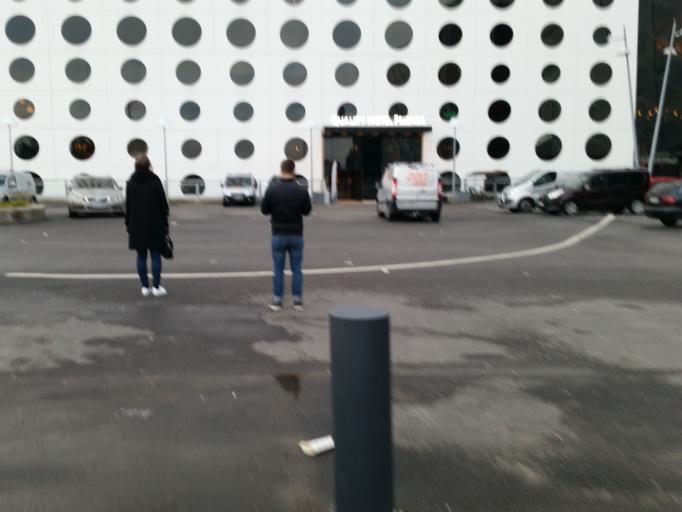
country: SE
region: Stockholm
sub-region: Solna Kommun
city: Solna
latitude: 59.3726
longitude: 18.0026
